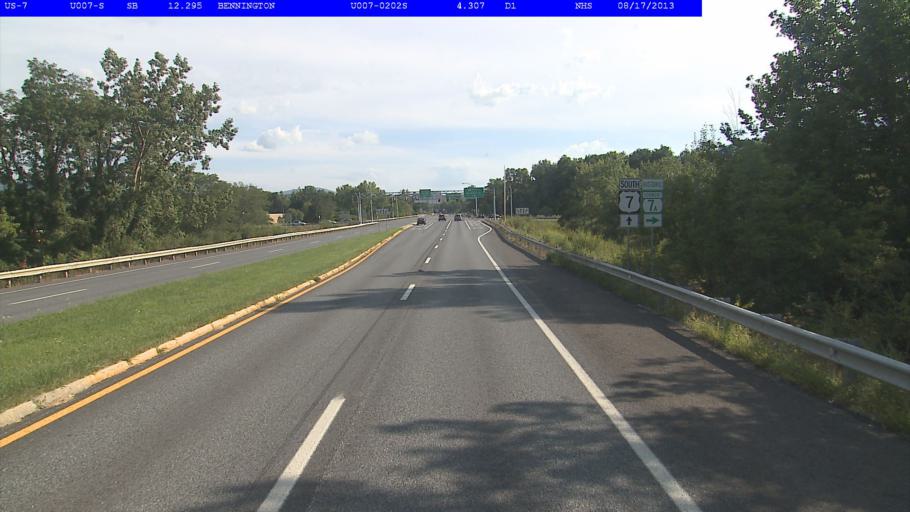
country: US
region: Vermont
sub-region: Bennington County
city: Bennington
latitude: 42.8958
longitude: -73.2000
